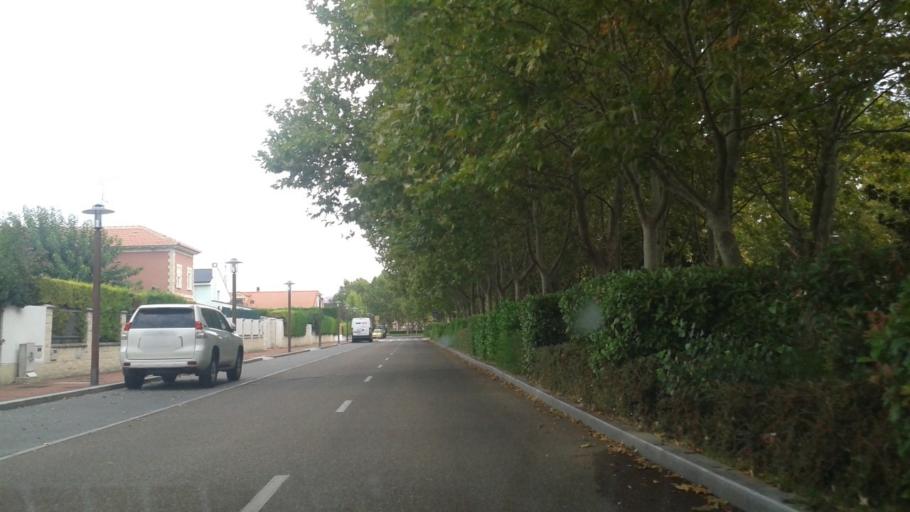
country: ES
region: Castille and Leon
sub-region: Provincia de Valladolid
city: Arroyo
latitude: 41.6148
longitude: -4.7825
